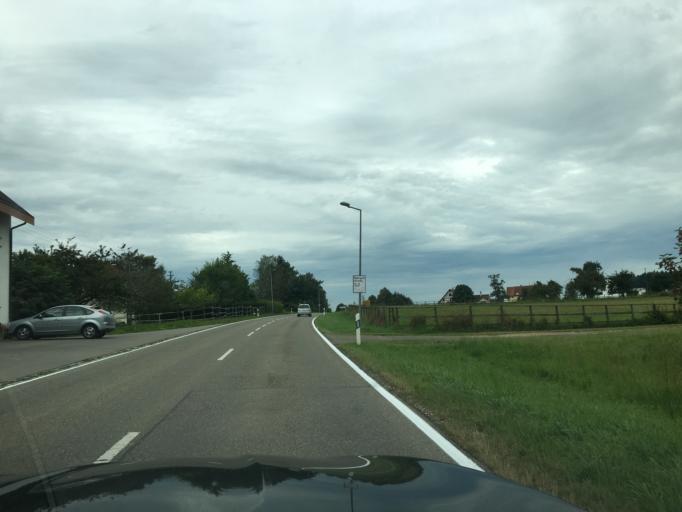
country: DE
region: Baden-Wuerttemberg
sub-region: Tuebingen Region
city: Rot
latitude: 47.8824
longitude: 9.1399
